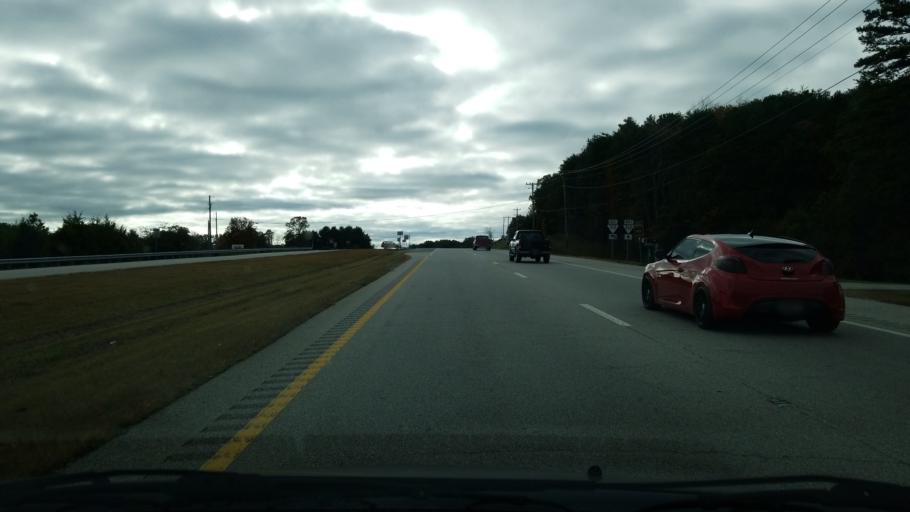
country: US
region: Tennessee
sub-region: Hamilton County
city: Lakesite
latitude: 35.1865
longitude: -85.0580
